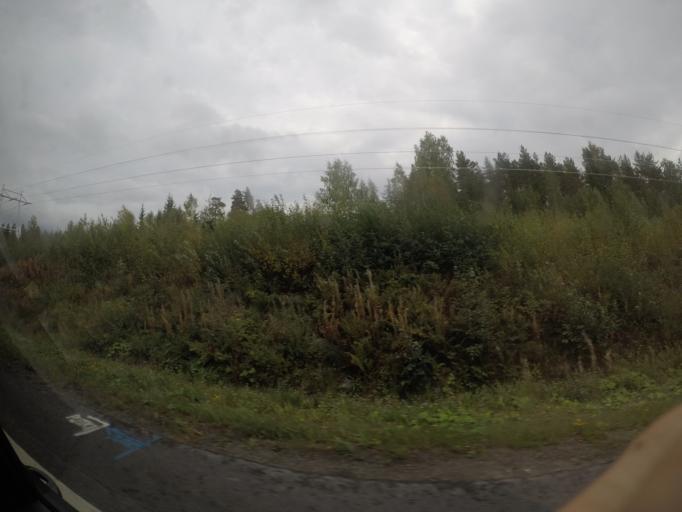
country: FI
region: Haeme
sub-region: Haemeenlinna
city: Parola
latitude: 61.1300
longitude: 24.4181
